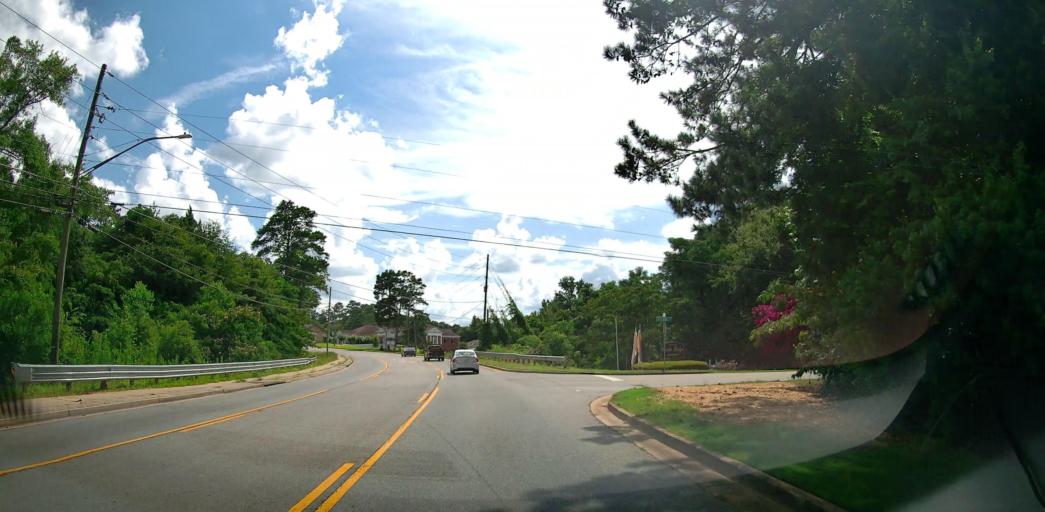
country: US
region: Georgia
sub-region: Houston County
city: Centerville
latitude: 32.6137
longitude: -83.6516
